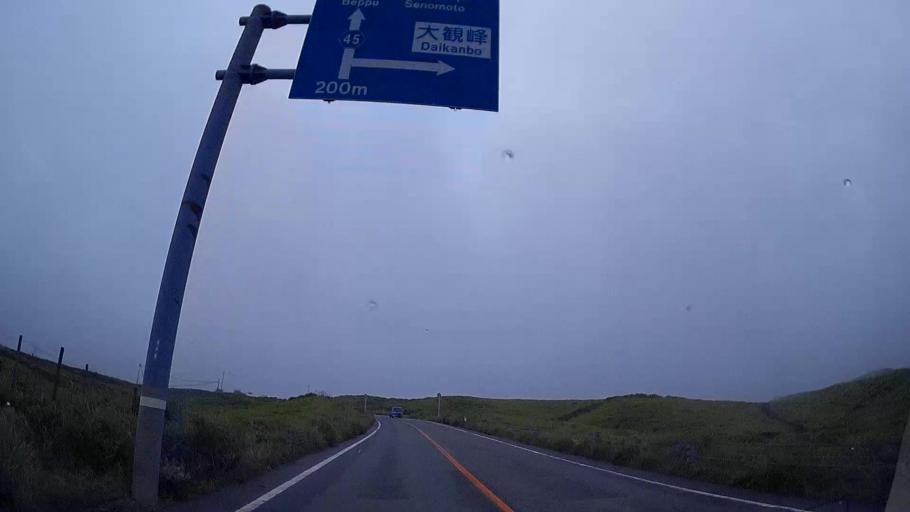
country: JP
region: Kumamoto
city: Aso
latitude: 33.0026
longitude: 131.0711
